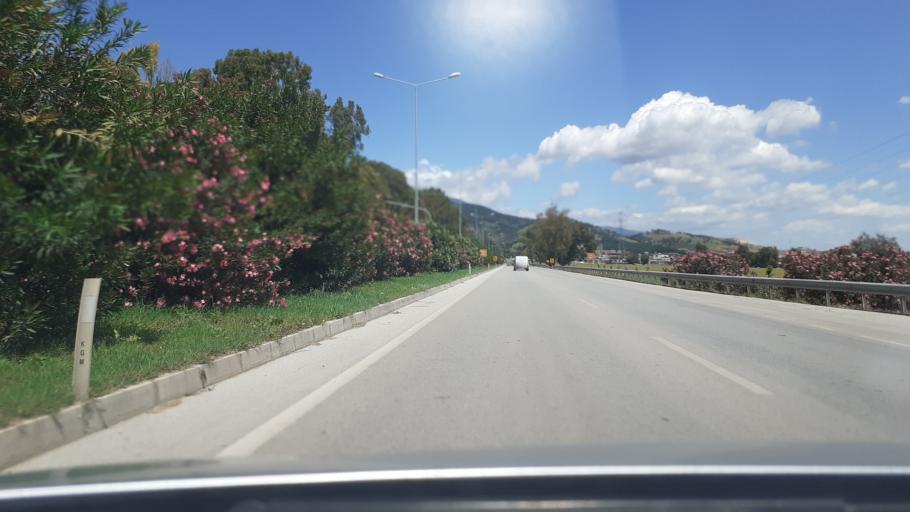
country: TR
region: Hatay
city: Serinyol
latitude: 36.3799
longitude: 36.2287
